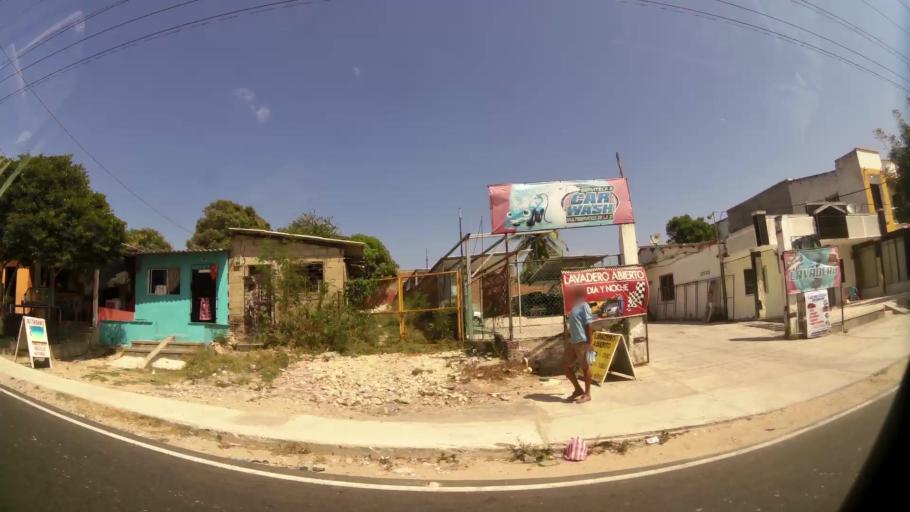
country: CO
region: Atlantico
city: Barranquilla
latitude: 10.9712
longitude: -74.8256
